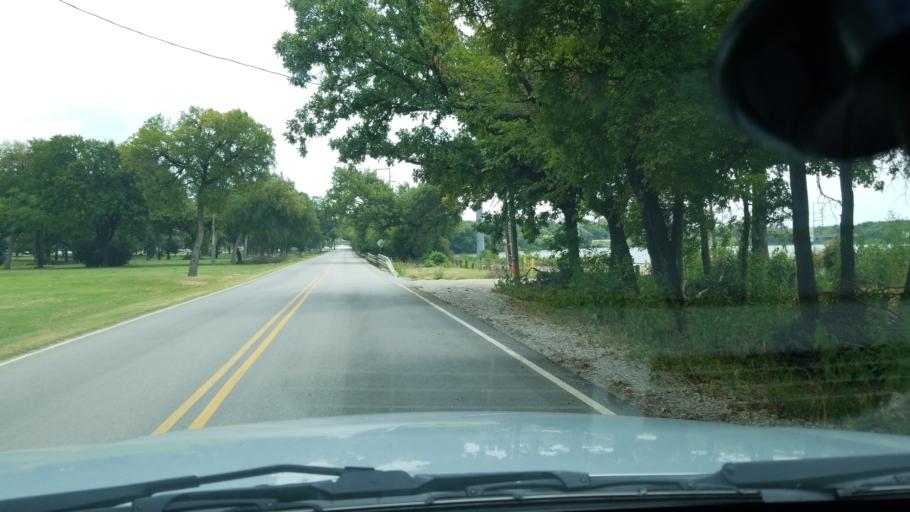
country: US
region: Texas
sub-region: Dallas County
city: Irving
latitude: 32.8668
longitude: -96.9231
